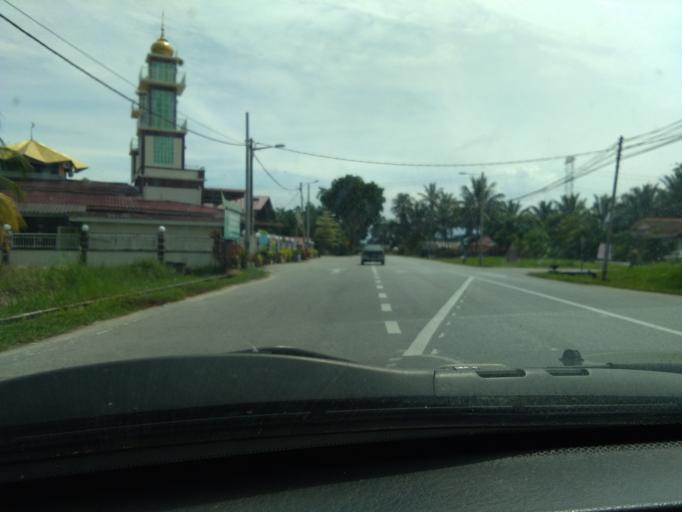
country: MY
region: Perak
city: Bagan Serai
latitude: 5.0518
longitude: 100.5883
